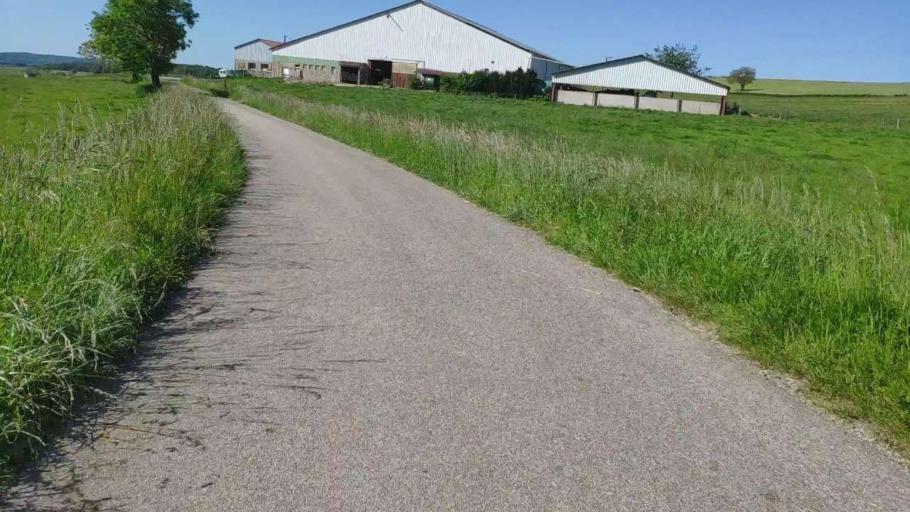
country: FR
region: Franche-Comte
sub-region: Departement du Jura
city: Perrigny
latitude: 46.7216
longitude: 5.5738
